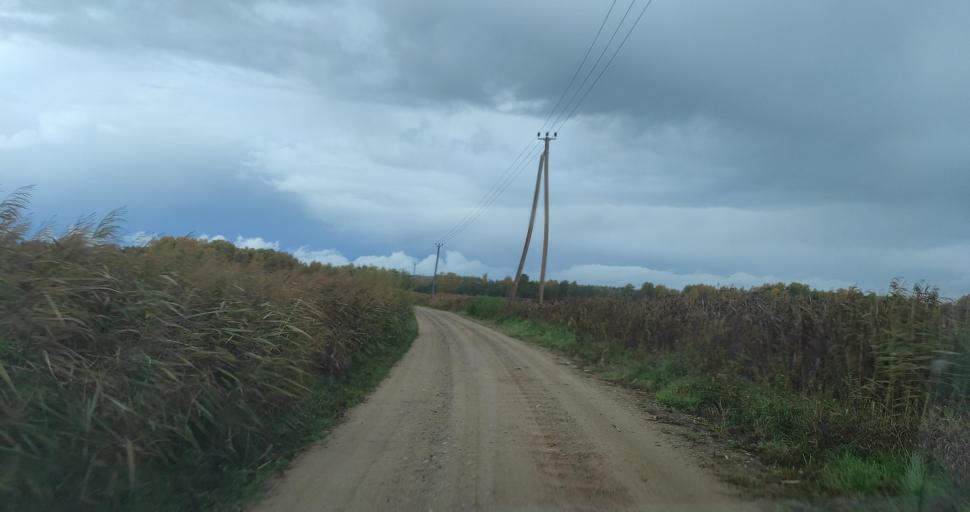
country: LV
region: Skrunda
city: Skrunda
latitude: 56.6865
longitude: 21.9871
